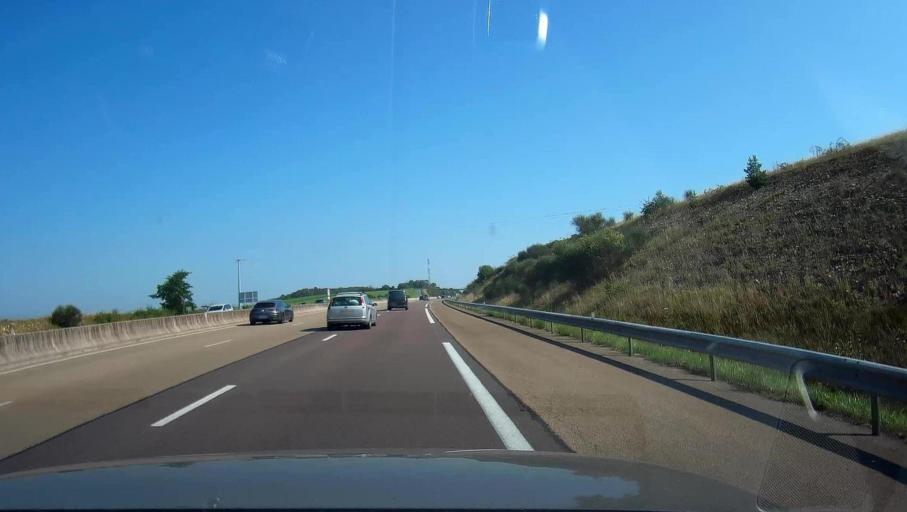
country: FR
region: Bourgogne
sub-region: Departement de la Cote-d'Or
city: Saint-Julien
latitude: 47.4453
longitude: 5.1683
